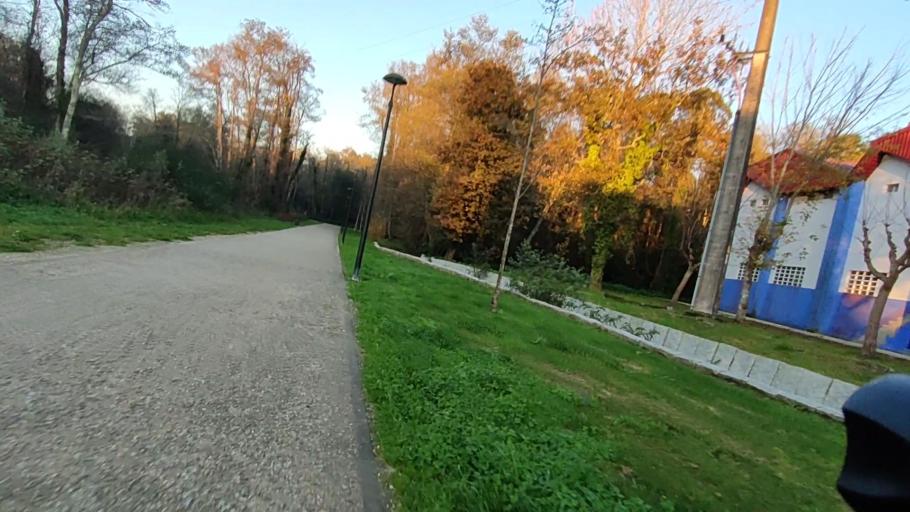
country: ES
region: Galicia
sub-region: Provincia da Coruna
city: Boiro
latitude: 42.6401
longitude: -8.8798
